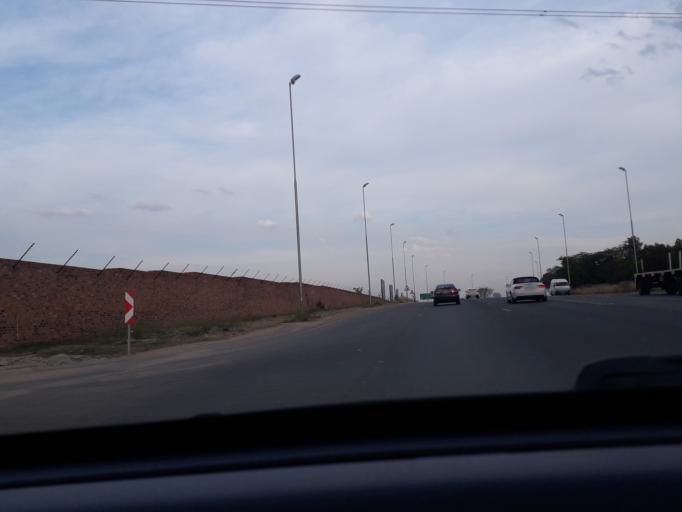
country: ZA
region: Gauteng
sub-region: City of Johannesburg Metropolitan Municipality
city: Diepsloot
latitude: -25.9841
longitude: 27.9805
